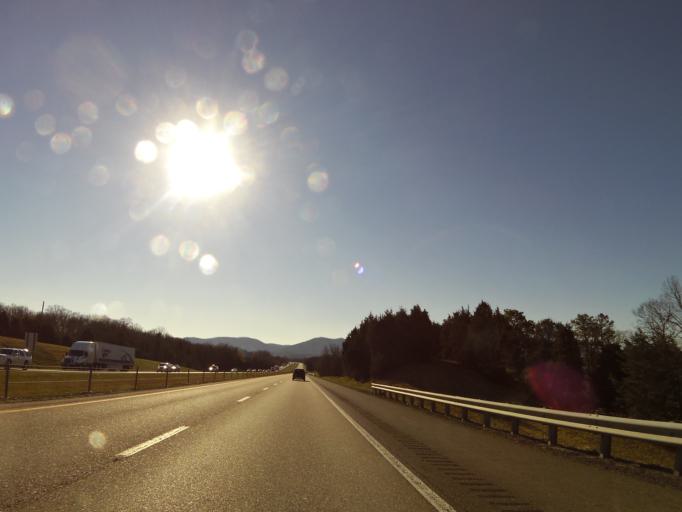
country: US
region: Tennessee
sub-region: Jefferson County
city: White Pine
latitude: 36.0027
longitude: -83.2900
